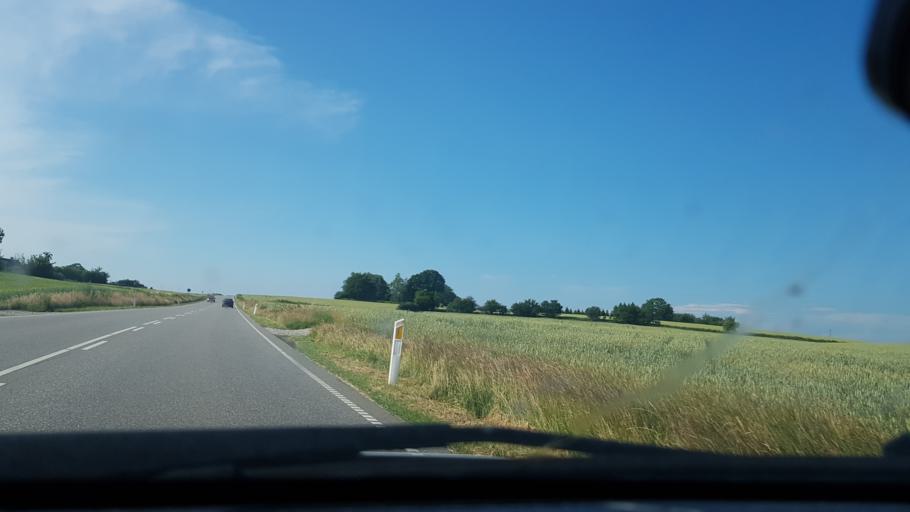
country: DK
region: Zealand
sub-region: Odsherred Kommune
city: Hojby
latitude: 55.8522
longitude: 11.5939
